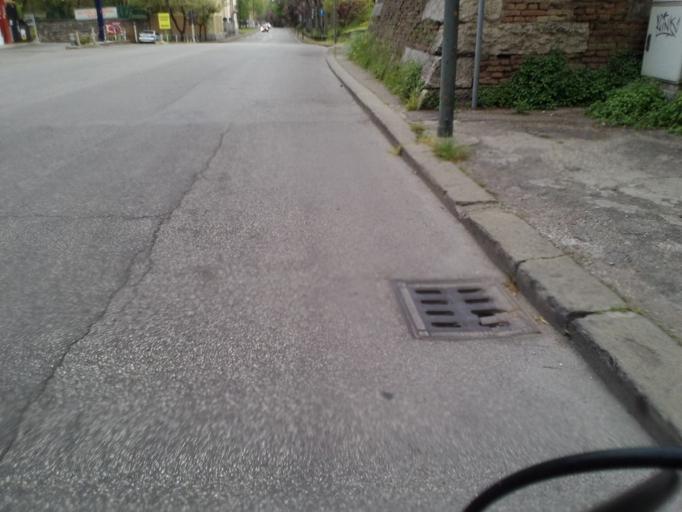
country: IT
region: Veneto
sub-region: Provincia di Verona
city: Verona
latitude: 45.4400
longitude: 10.9772
